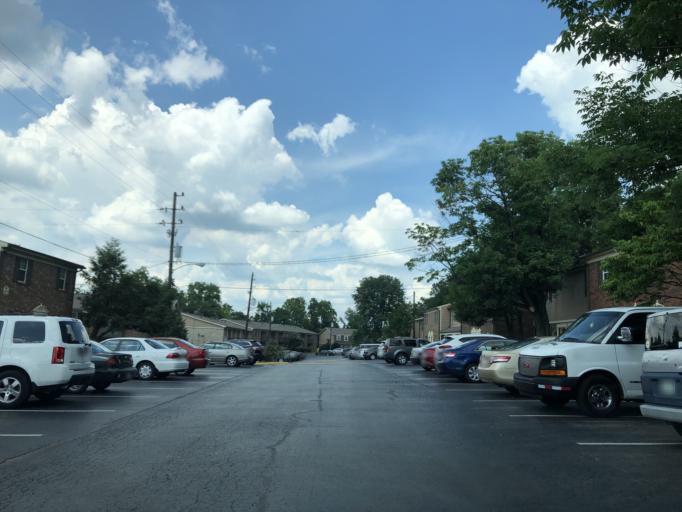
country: US
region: Tennessee
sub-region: Davidson County
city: Nashville
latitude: 36.1301
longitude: -86.7237
